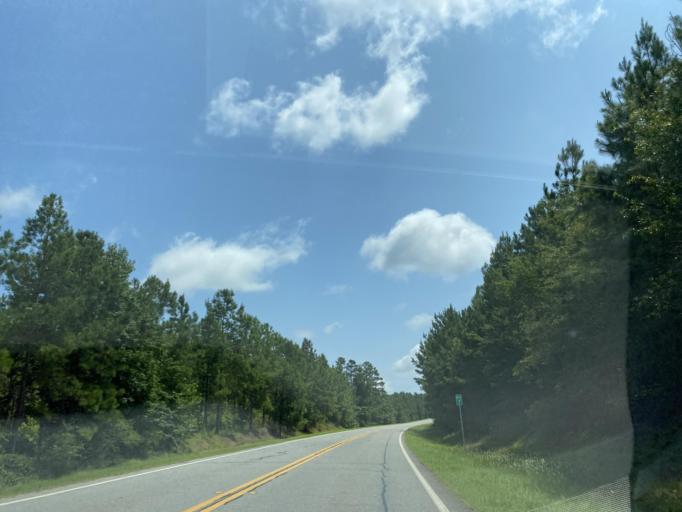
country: US
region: Georgia
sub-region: Wilcox County
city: Abbeville
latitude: 32.0046
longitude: -83.1682
